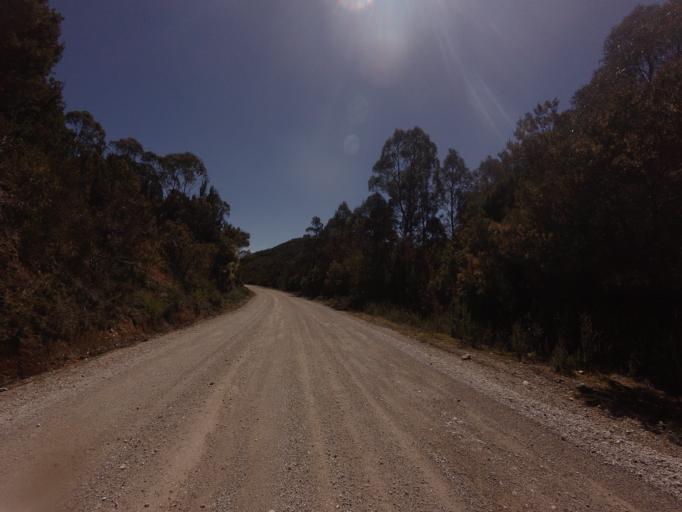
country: AU
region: Tasmania
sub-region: Huon Valley
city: Geeveston
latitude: -42.8217
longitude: 146.3901
